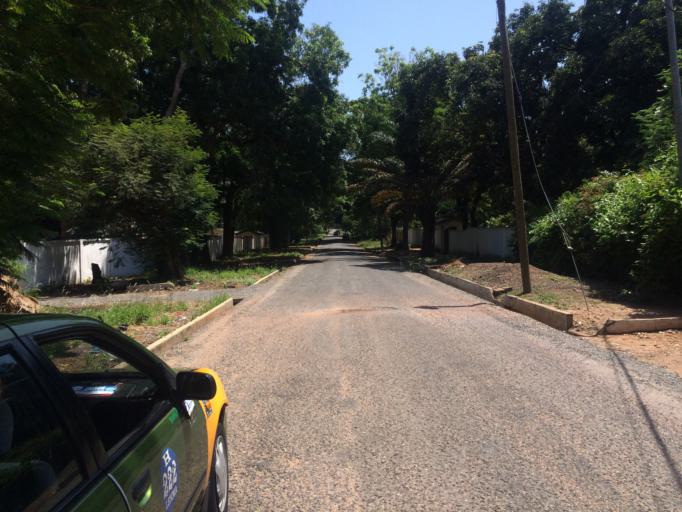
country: GH
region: Greater Accra
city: Accra
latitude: 5.5642
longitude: -0.1901
